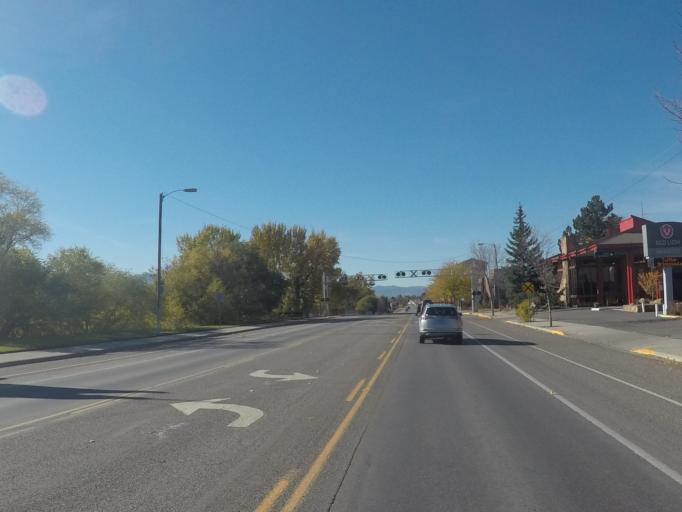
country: US
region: Montana
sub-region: Missoula County
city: Missoula
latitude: 46.8750
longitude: -114.0035
